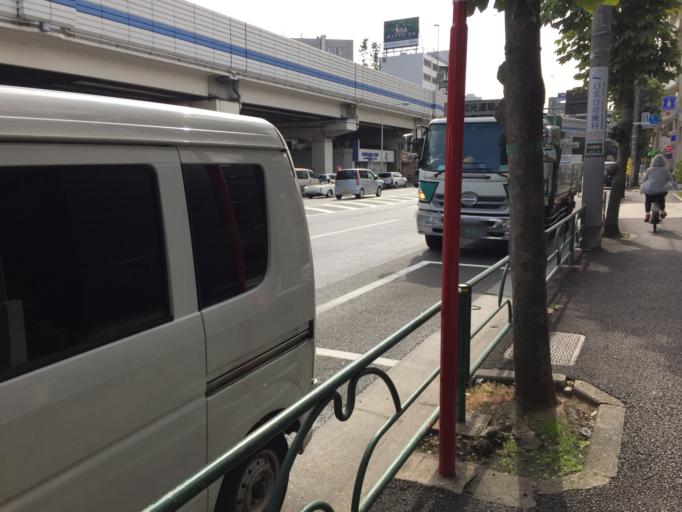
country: JP
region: Tokyo
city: Tokyo
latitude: 35.6445
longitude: 139.7215
